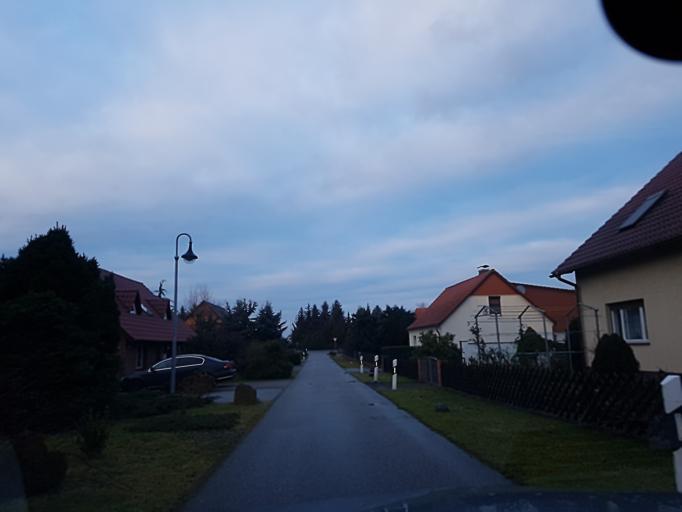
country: DE
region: Brandenburg
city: Schilda
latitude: 51.5847
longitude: 13.3887
